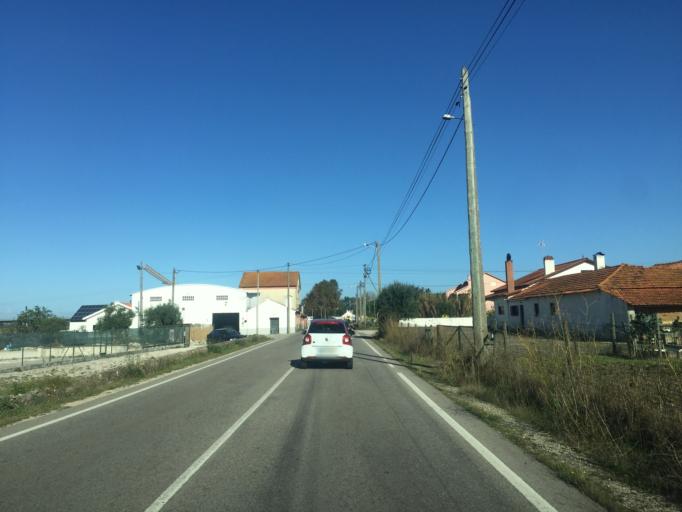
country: PT
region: Leiria
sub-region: Leiria
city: Amor
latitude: 39.8010
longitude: -8.8383
